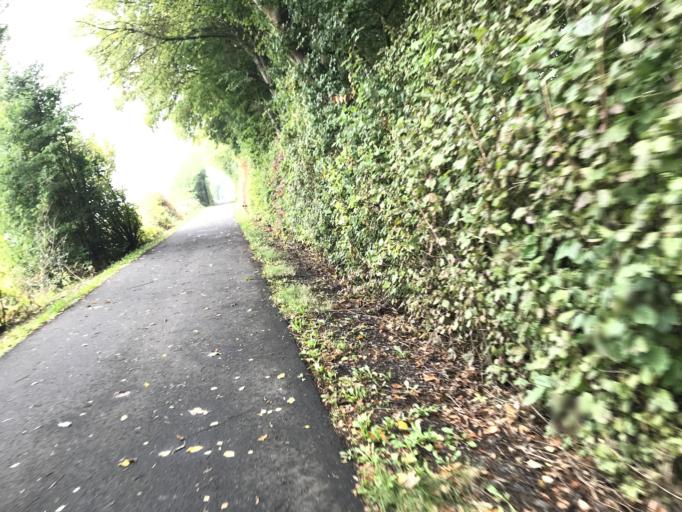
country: DE
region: Hesse
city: Gudensberg
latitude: 51.1894
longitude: 9.3993
